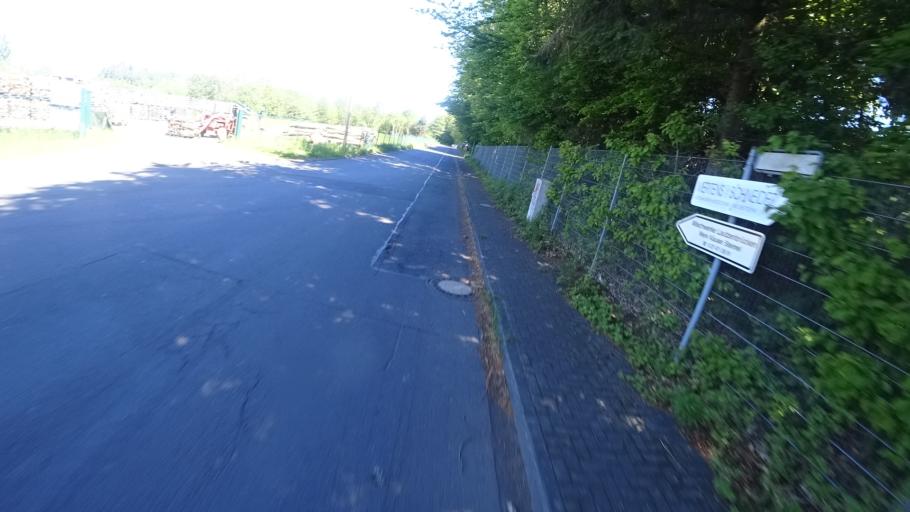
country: DE
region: Rheinland-Pfalz
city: Elkenroth
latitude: 50.7360
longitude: 7.8827
